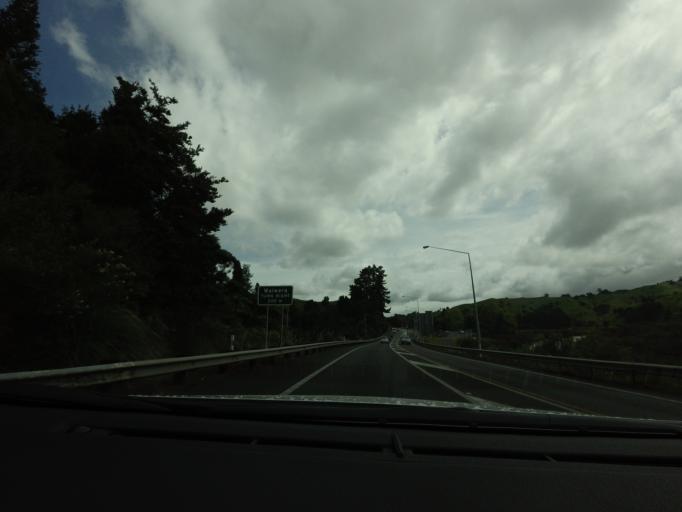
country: NZ
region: Auckland
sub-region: Auckland
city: Warkworth
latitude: -36.5239
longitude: 174.6763
